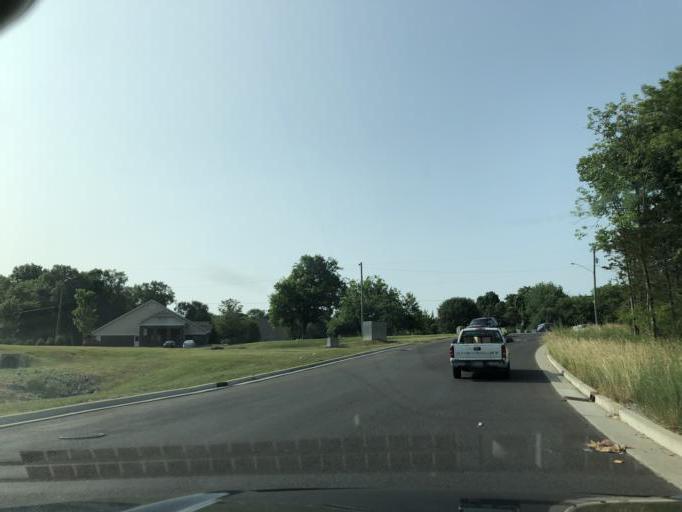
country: US
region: Tennessee
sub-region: Rutherford County
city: La Vergne
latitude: 36.0496
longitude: -86.6379
